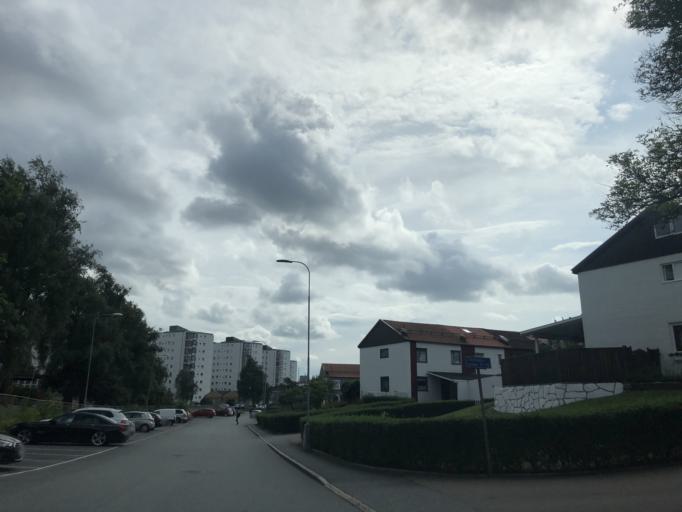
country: SE
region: Vaestra Goetaland
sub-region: Goteborg
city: Majorna
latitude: 57.7141
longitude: 11.8869
